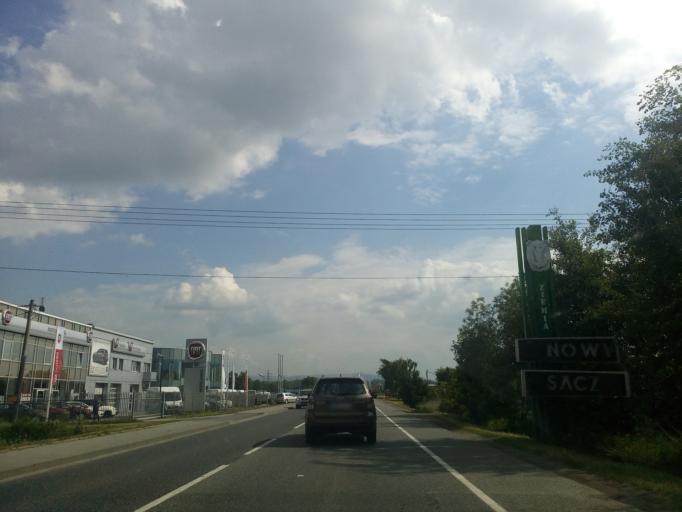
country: PL
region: Lesser Poland Voivodeship
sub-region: Powiat nowosadecki
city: Chelmiec
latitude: 49.6633
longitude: 20.6889
